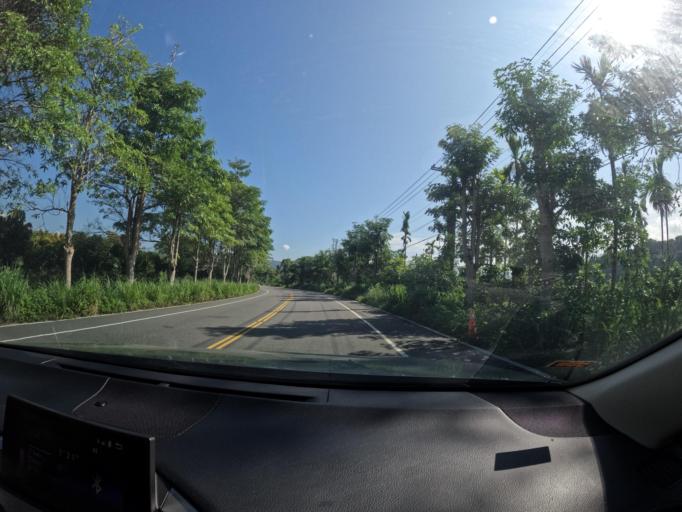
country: TW
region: Taiwan
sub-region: Hualien
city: Hualian
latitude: 23.4845
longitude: 121.3728
